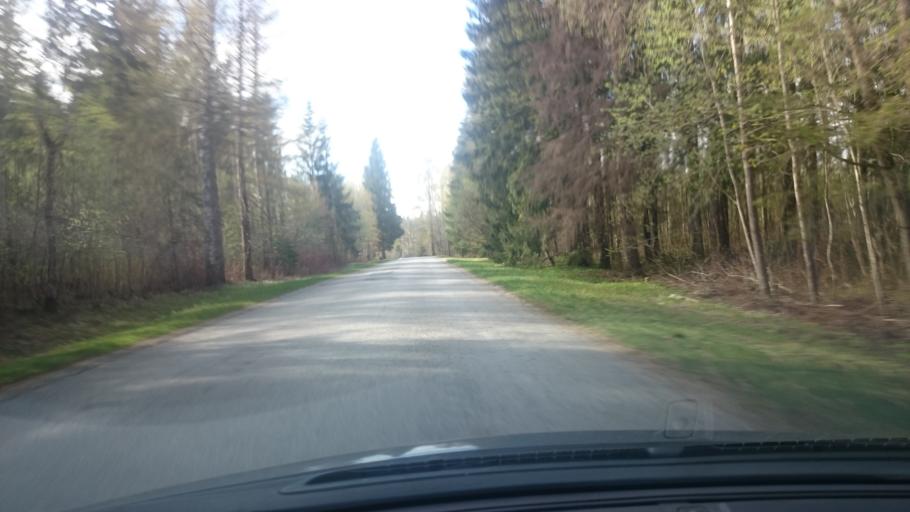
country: EE
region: Ida-Virumaa
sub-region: Toila vald
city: Voka
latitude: 59.1635
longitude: 27.5871
